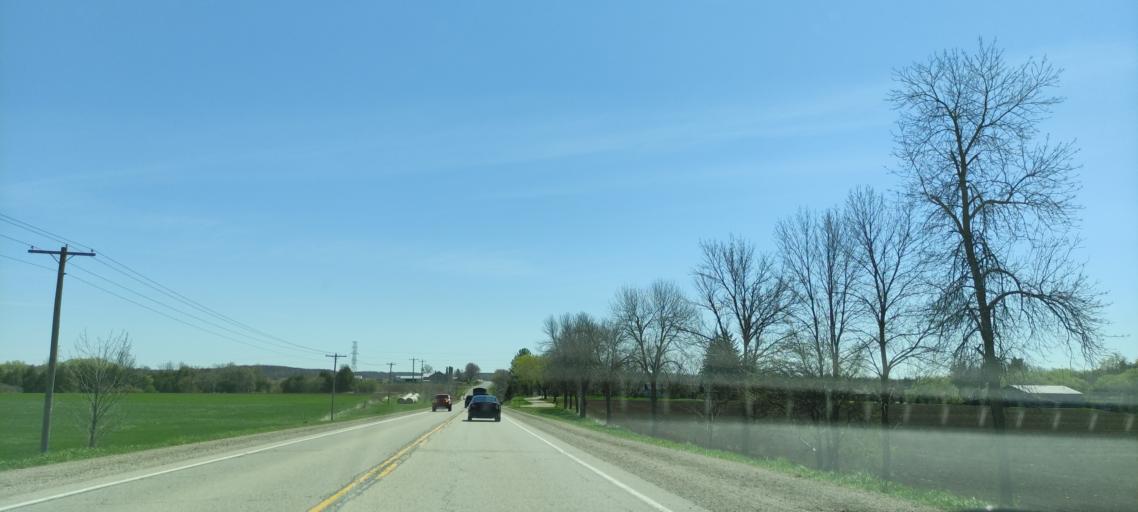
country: CA
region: Ontario
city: Waterloo
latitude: 43.5850
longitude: -80.4510
